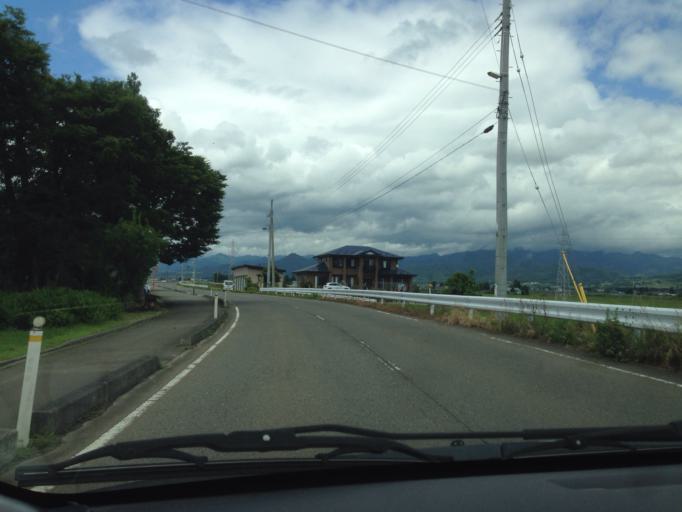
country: JP
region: Fukushima
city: Kitakata
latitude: 37.6159
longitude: 139.8996
